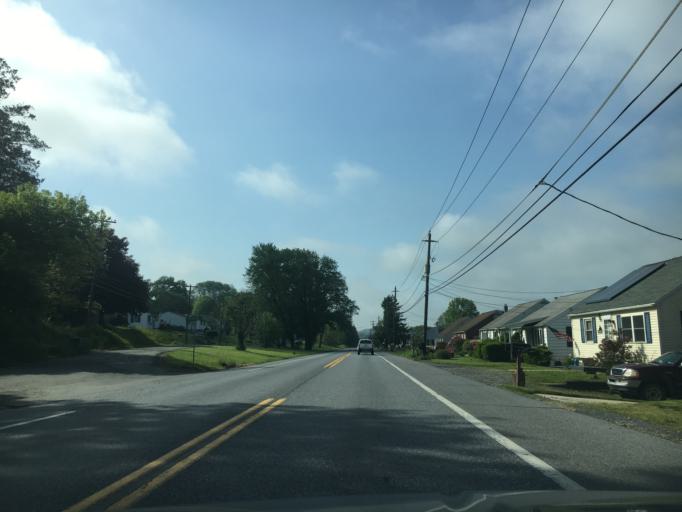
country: US
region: Pennsylvania
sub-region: Berks County
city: Boyertown
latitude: 40.3477
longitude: -75.6616
